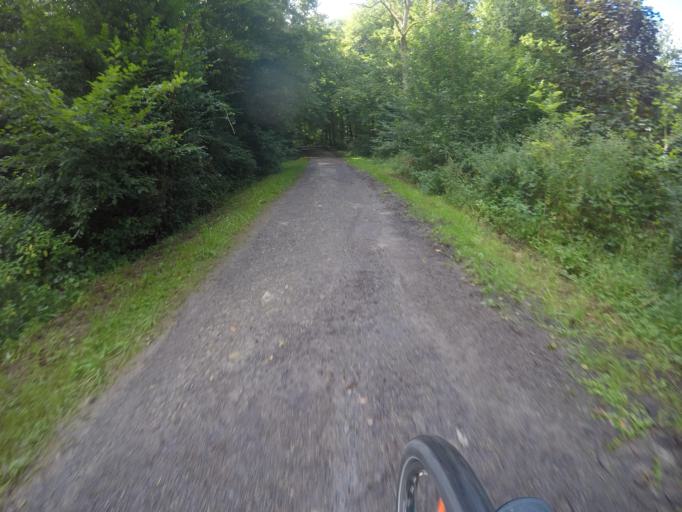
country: DE
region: Baden-Wuerttemberg
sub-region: Regierungsbezirk Stuttgart
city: Ehningen
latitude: 48.6718
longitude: 8.9525
